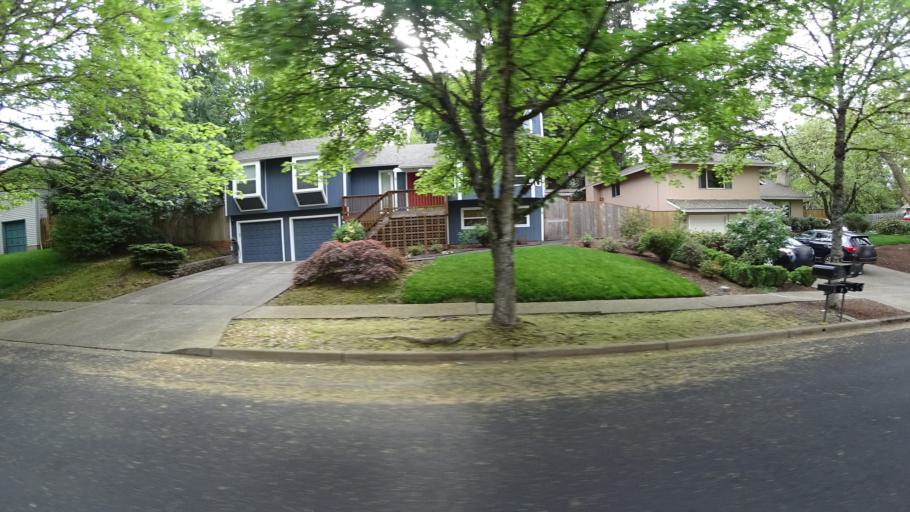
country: US
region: Oregon
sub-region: Washington County
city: Beaverton
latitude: 45.4513
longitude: -122.8231
